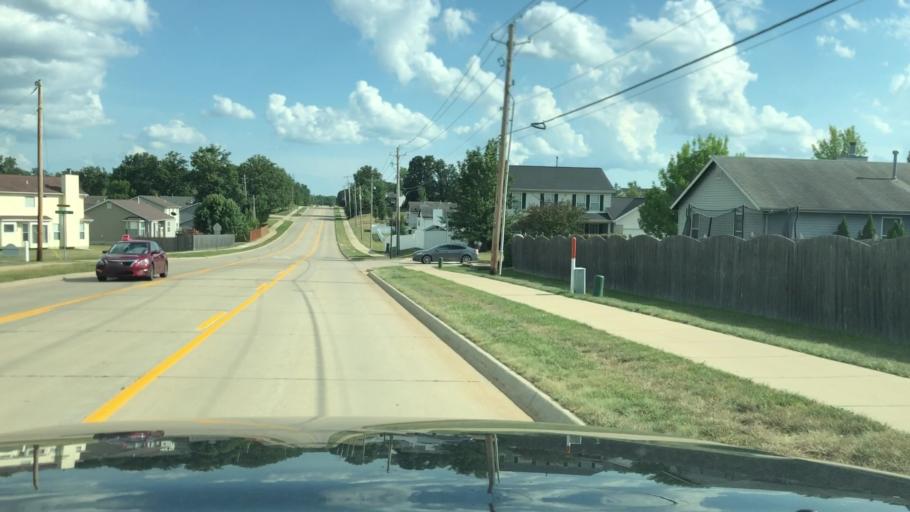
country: US
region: Missouri
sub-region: Saint Charles County
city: Wentzville
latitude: 38.8347
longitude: -90.8922
